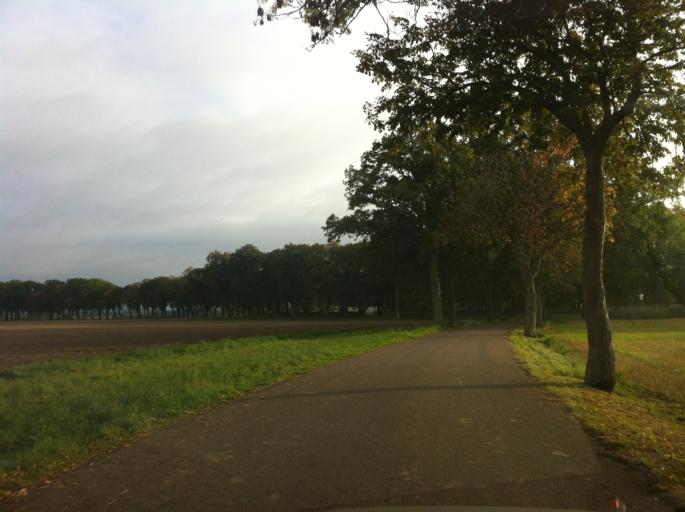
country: SE
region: Skane
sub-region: Helsingborg
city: Glumslov
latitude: 55.9750
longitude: 12.8921
